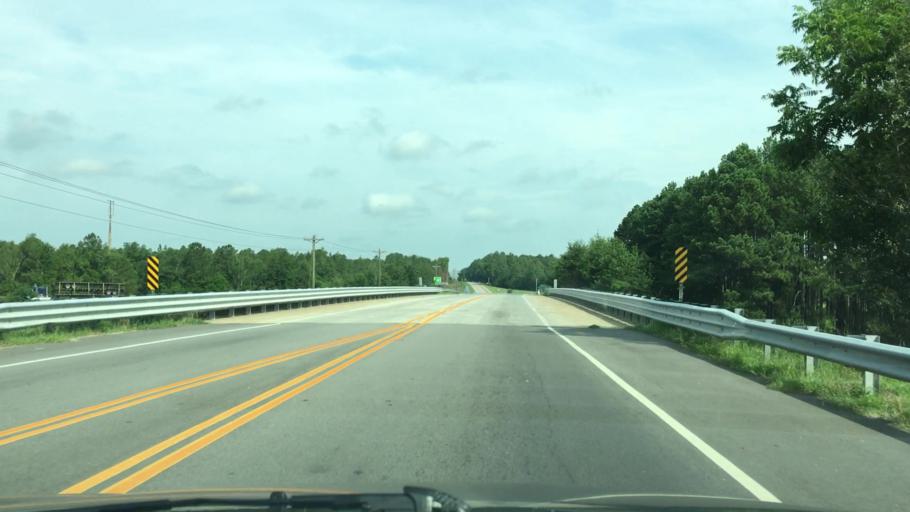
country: US
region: South Carolina
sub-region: Lexington County
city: Batesburg
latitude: 33.7518
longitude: -81.5271
